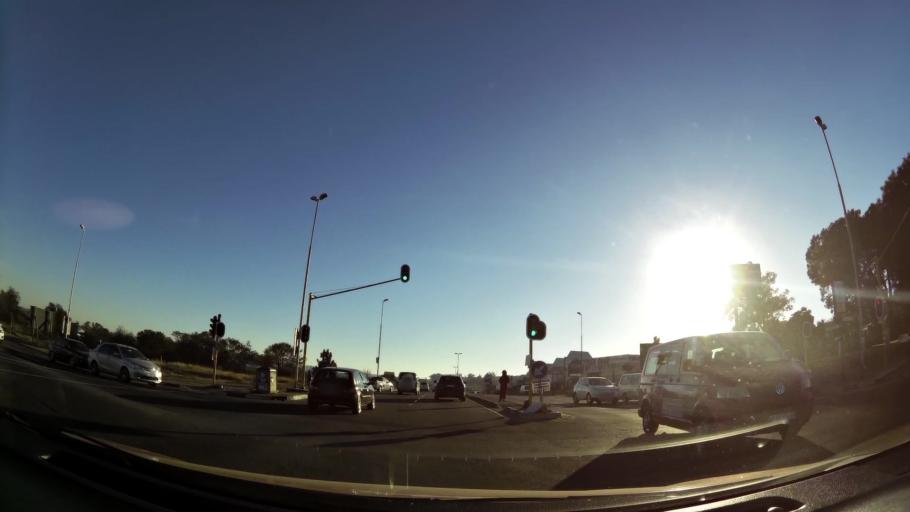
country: ZA
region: Gauteng
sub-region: City of Johannesburg Metropolitan Municipality
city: Midrand
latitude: -26.0095
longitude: 28.1212
